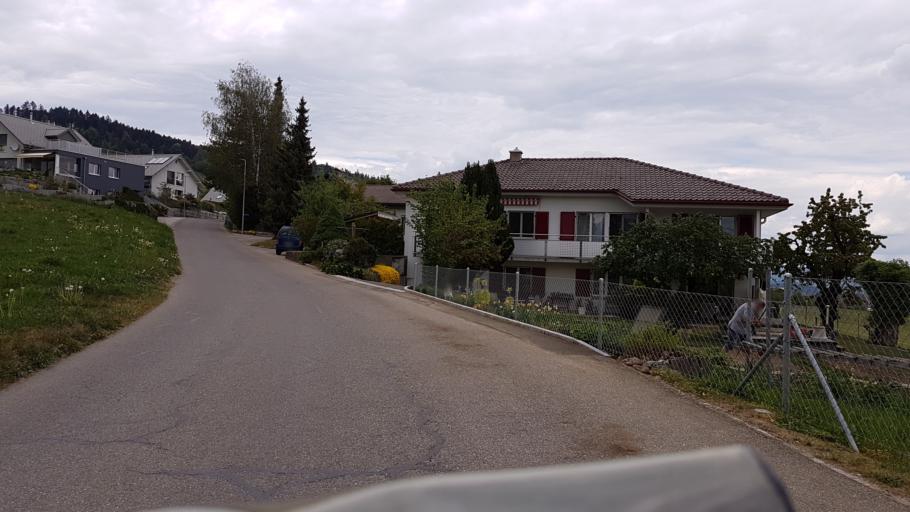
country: CH
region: Bern
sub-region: Bern-Mittelland District
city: Niederwichtrach
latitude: 46.8408
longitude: 7.5505
